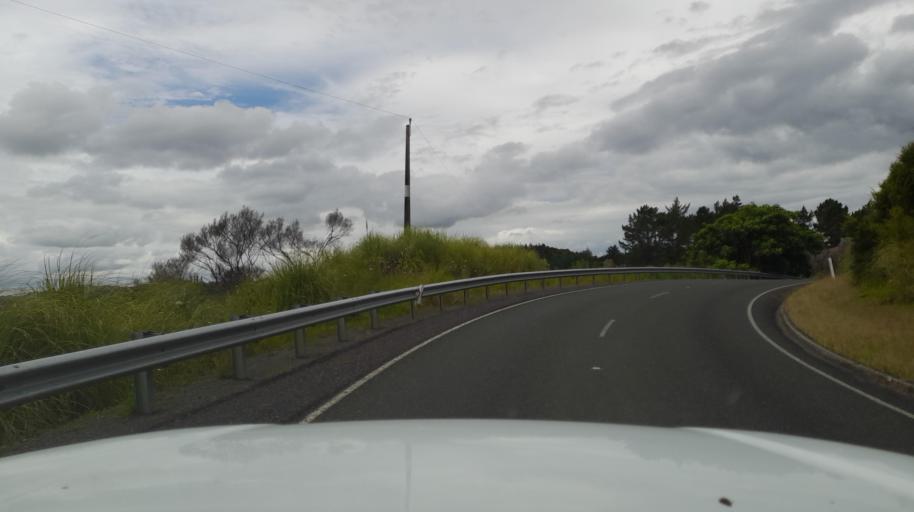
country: NZ
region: Northland
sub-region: Far North District
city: Kaitaia
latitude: -35.3699
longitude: 173.4169
